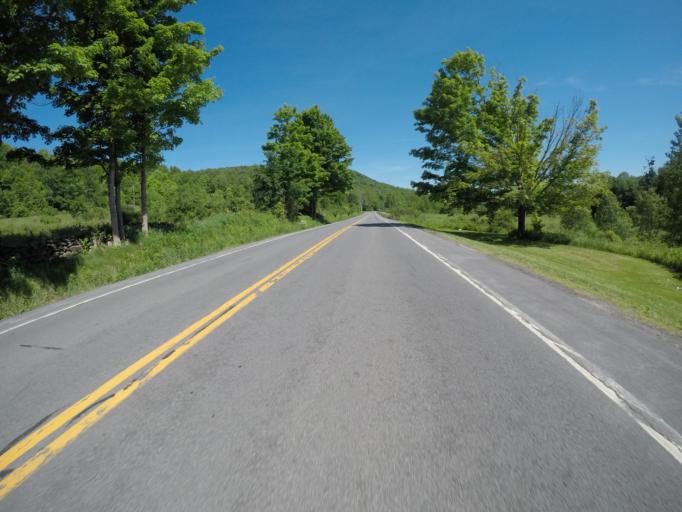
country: US
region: New York
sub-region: Delaware County
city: Delhi
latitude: 42.2269
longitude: -74.9700
